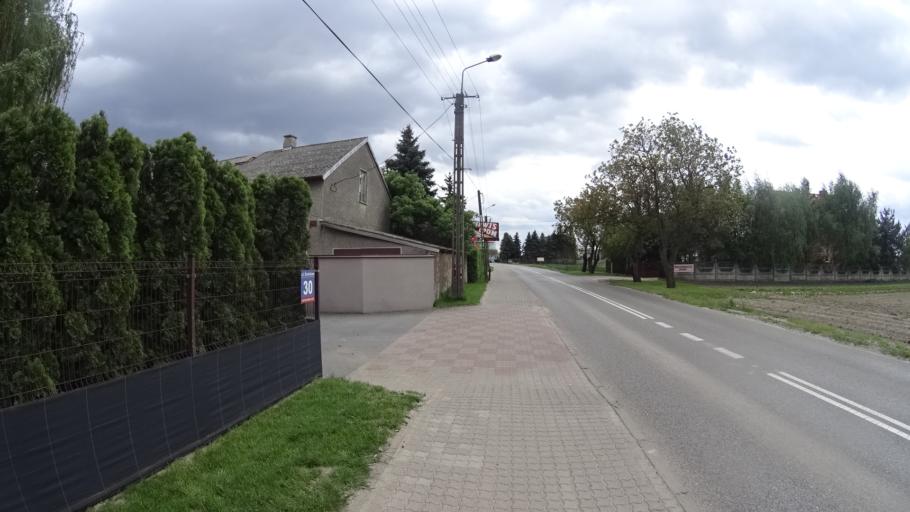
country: PL
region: Masovian Voivodeship
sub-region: Powiat warszawski zachodni
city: Babice
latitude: 52.2272
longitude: 20.8322
